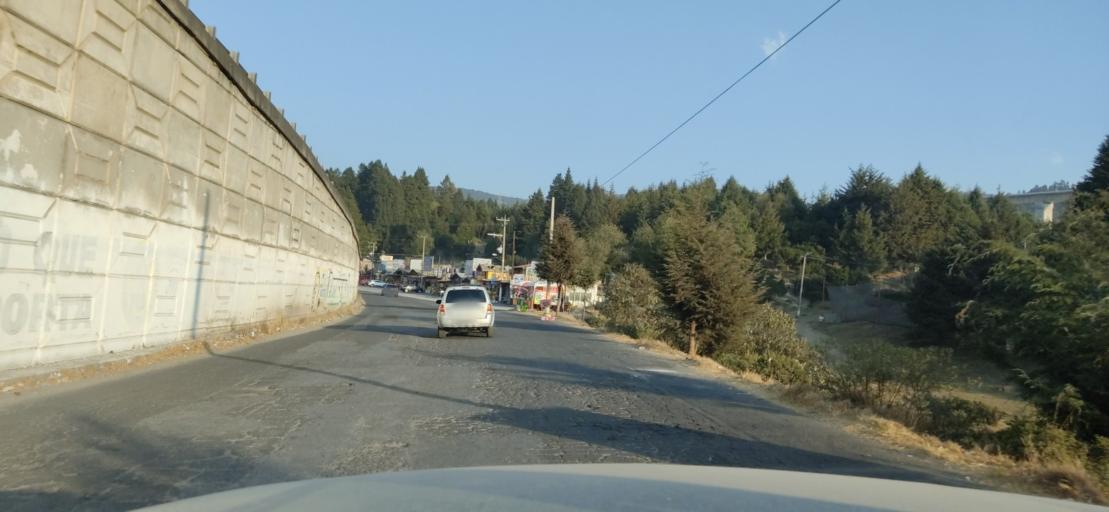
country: MX
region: Morelos
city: San Jeronimo Acazulco
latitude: 19.2980
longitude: -99.3720
